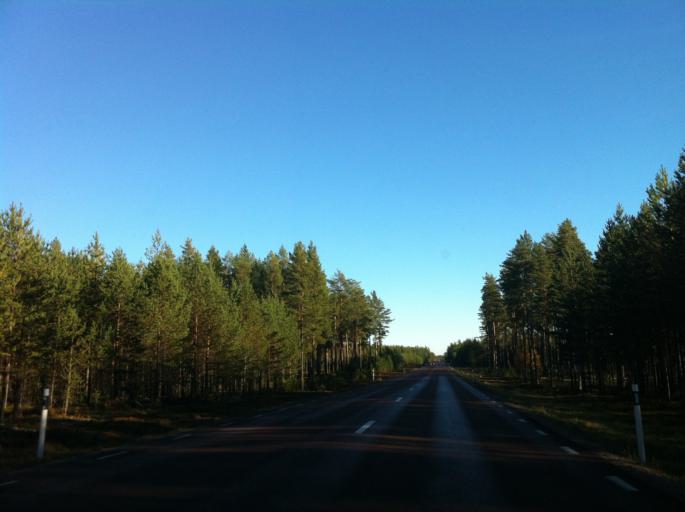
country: SE
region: Dalarna
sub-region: Leksand Municipality
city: Siljansnas
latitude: 60.9360
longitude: 14.7623
